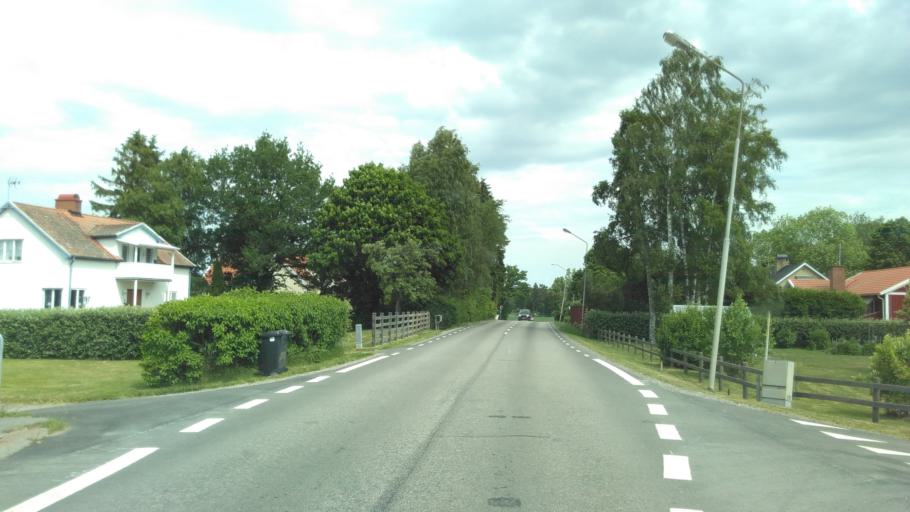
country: SE
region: Vaestra Goetaland
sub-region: Vara Kommun
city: Kvanum
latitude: 58.3836
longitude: 13.1482
